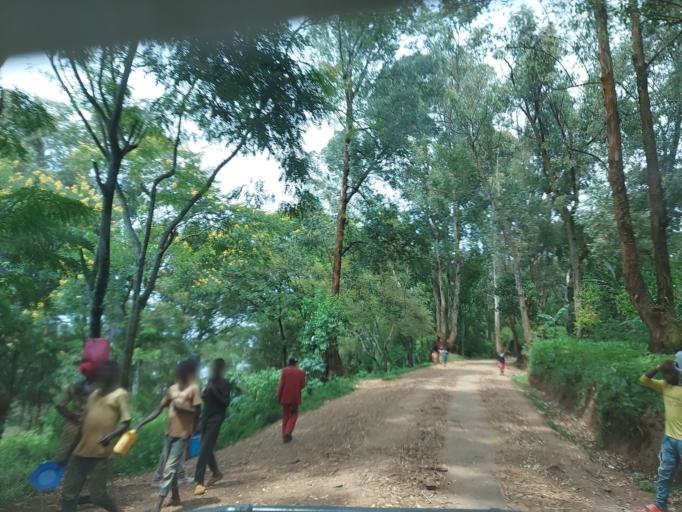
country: RW
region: Western Province
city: Cyangugu
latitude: -2.2343
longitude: 28.8579
